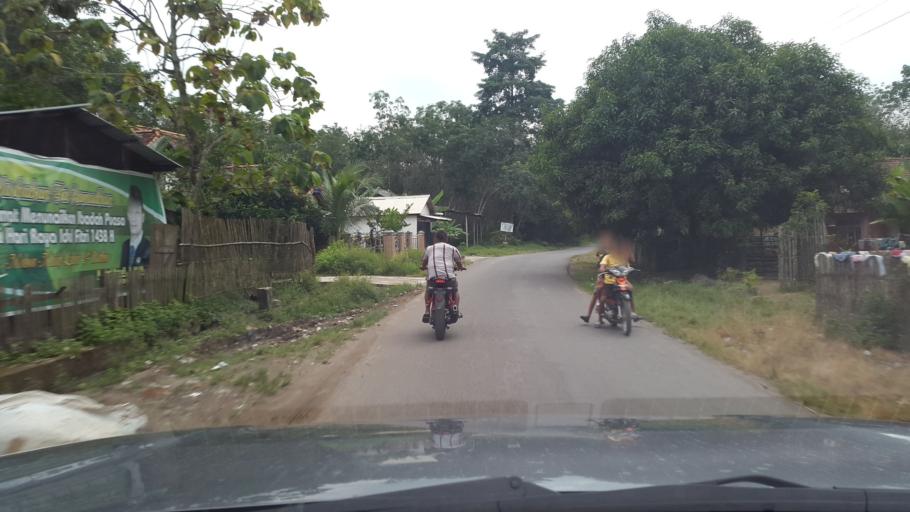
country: ID
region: South Sumatra
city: Gunungmenang
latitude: -3.2455
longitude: 104.0657
